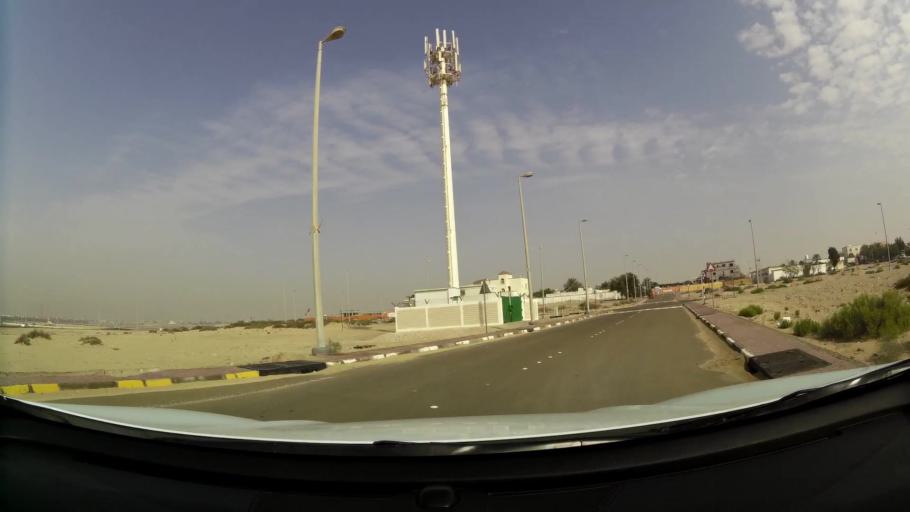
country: AE
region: Abu Dhabi
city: Abu Dhabi
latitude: 24.2641
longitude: 54.6917
